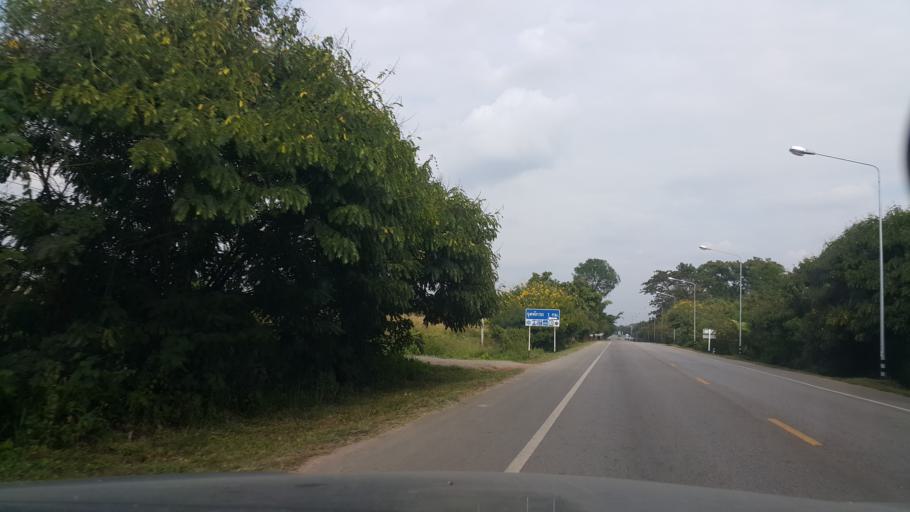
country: TH
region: Phayao
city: Phayao
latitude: 19.0921
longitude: 99.9064
